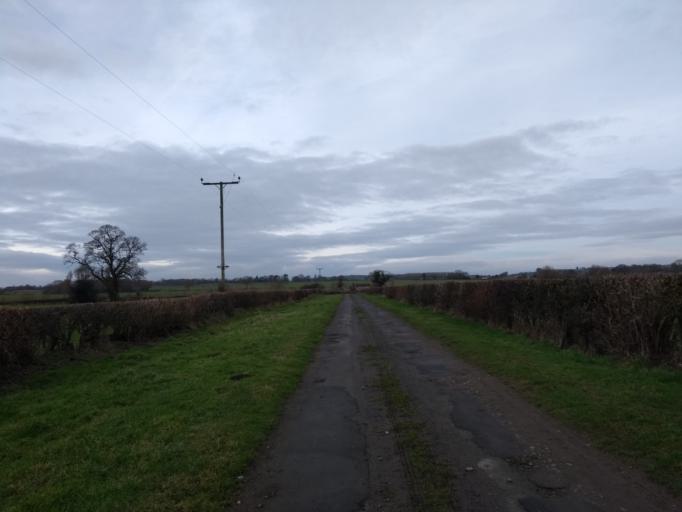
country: GB
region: England
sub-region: East Riding of Yorkshire
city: Stamford Bridge
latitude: 54.0663
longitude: -0.9321
